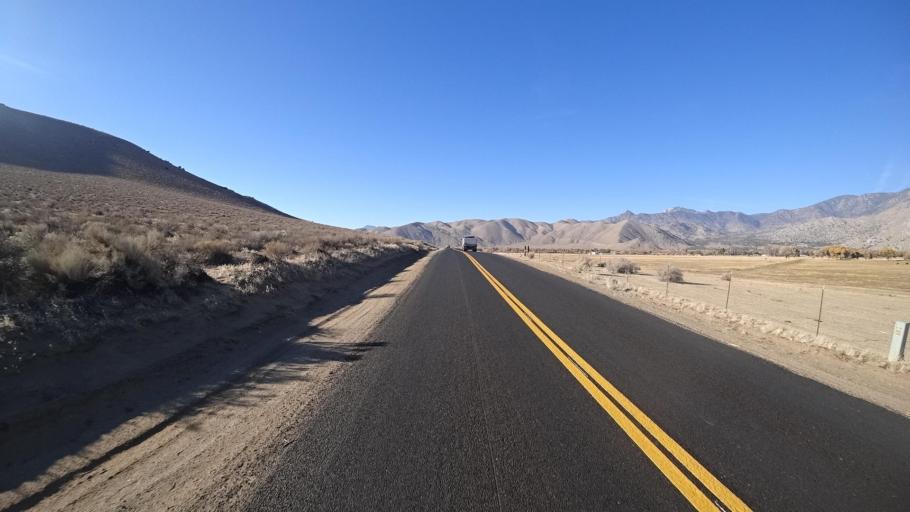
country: US
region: California
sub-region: Kern County
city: Weldon
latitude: 35.6581
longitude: -118.2899
